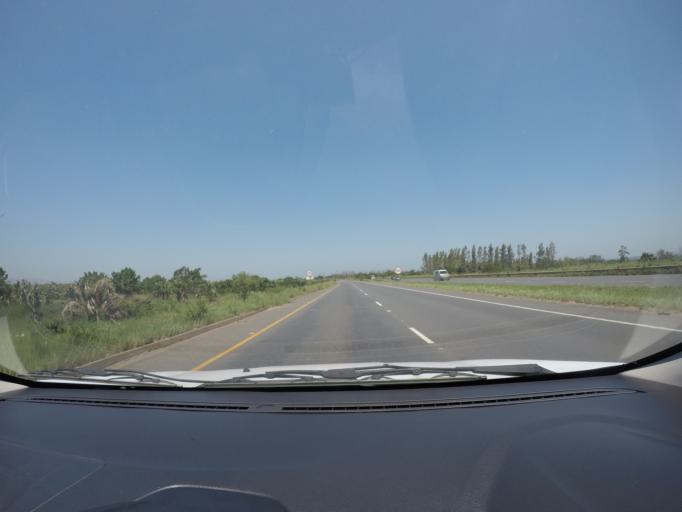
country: ZA
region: KwaZulu-Natal
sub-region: uThungulu District Municipality
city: Richards Bay
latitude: -28.7794
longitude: 31.9717
